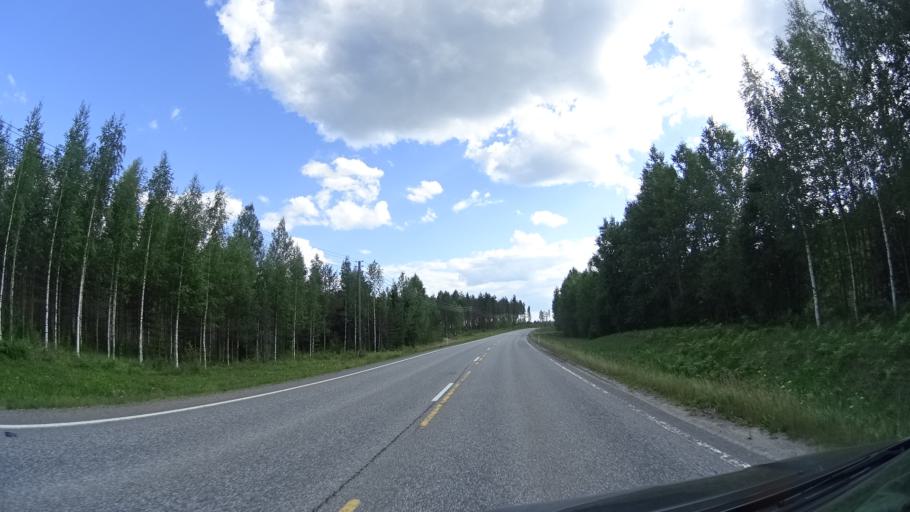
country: FI
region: Southern Savonia
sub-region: Savonlinna
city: Punkaharju
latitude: 61.6748
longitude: 29.4136
